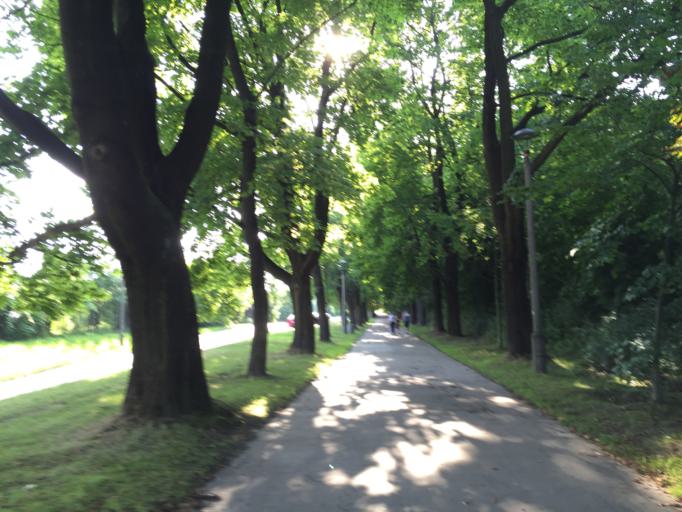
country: PL
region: Lesser Poland Voivodeship
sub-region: Krakow
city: Krakow
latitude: 50.0534
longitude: 19.8994
